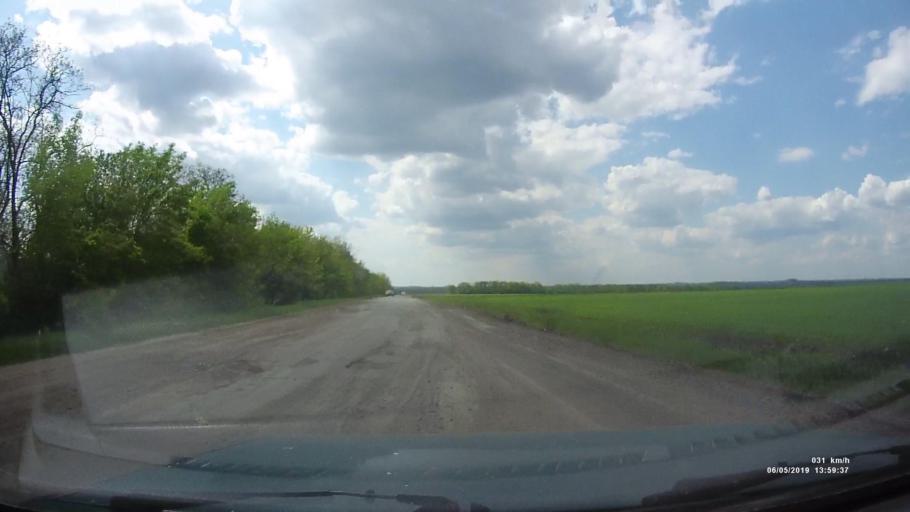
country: RU
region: Rostov
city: Shakhty
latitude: 47.6854
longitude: 40.3981
